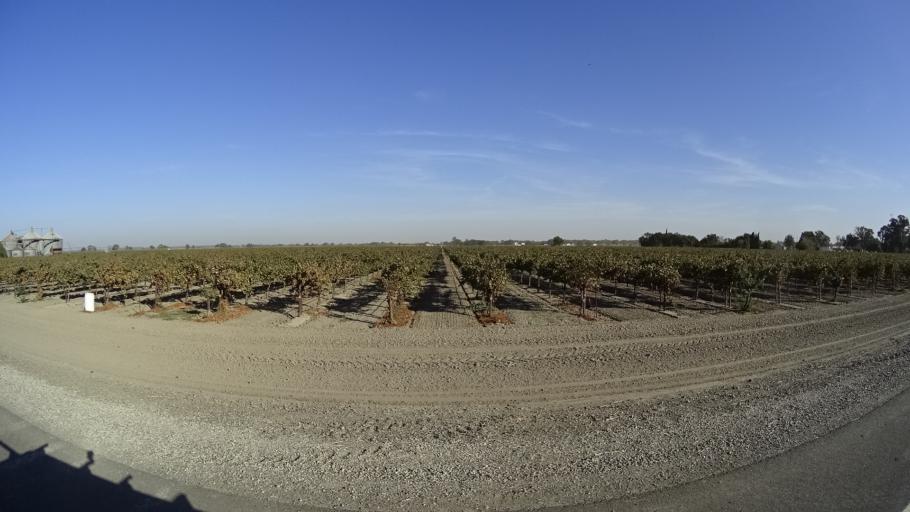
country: US
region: California
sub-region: Sacramento County
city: Parkway
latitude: 38.4143
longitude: -121.5445
